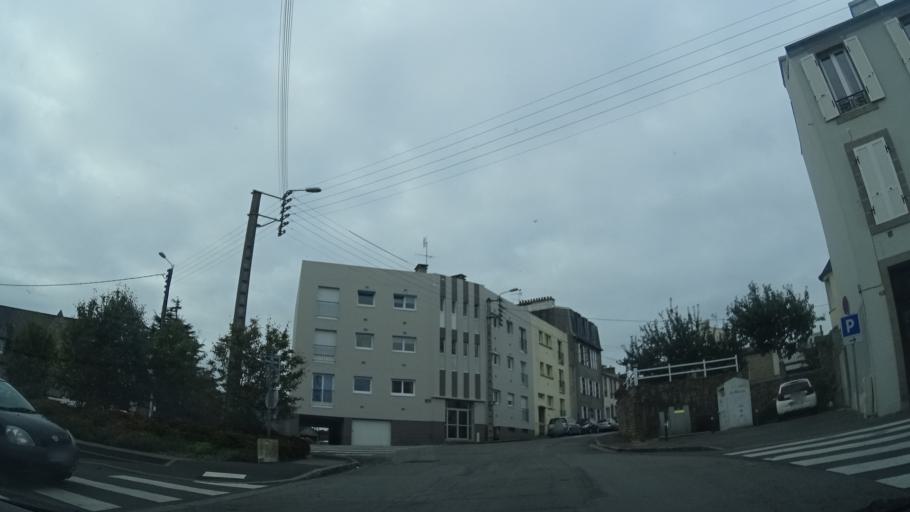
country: FR
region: Brittany
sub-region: Departement du Finistere
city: Brest
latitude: 48.3976
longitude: -4.4544
